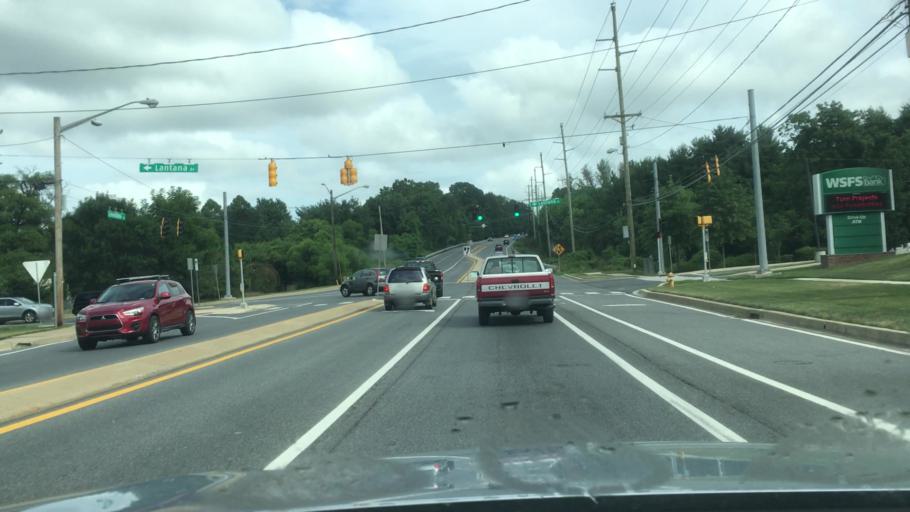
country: US
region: Delaware
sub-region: New Castle County
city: North Star
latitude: 39.7729
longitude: -75.7132
